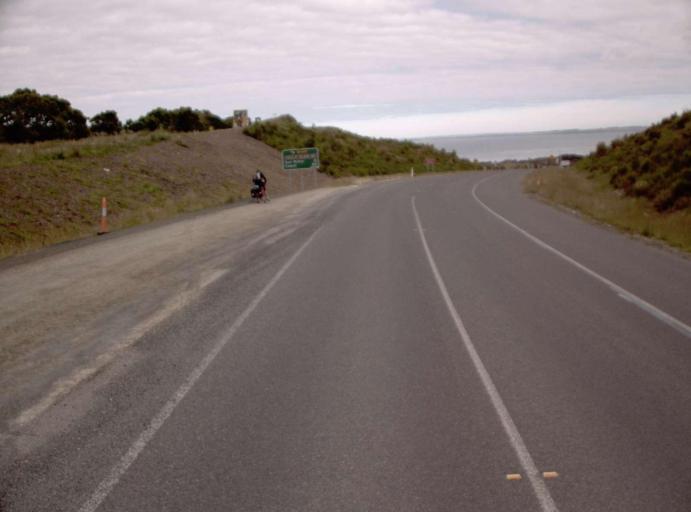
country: AU
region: Victoria
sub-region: Bass Coast
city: North Wonthaggi
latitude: -38.5255
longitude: 145.4342
